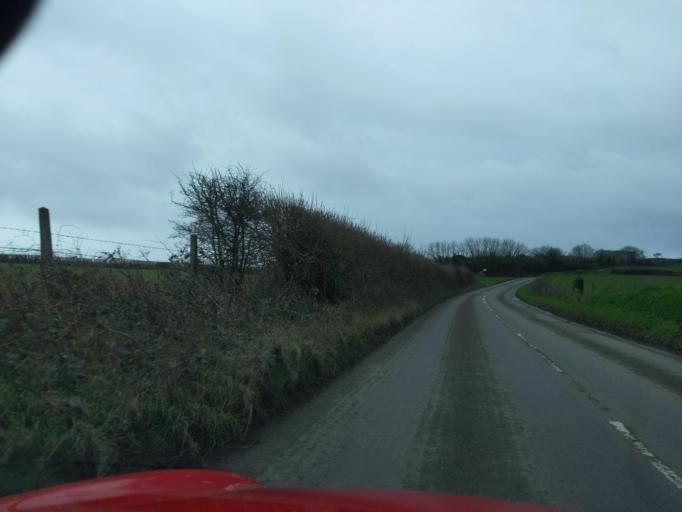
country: GB
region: England
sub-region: Devon
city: Modbury
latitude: 50.3319
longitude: -3.8725
